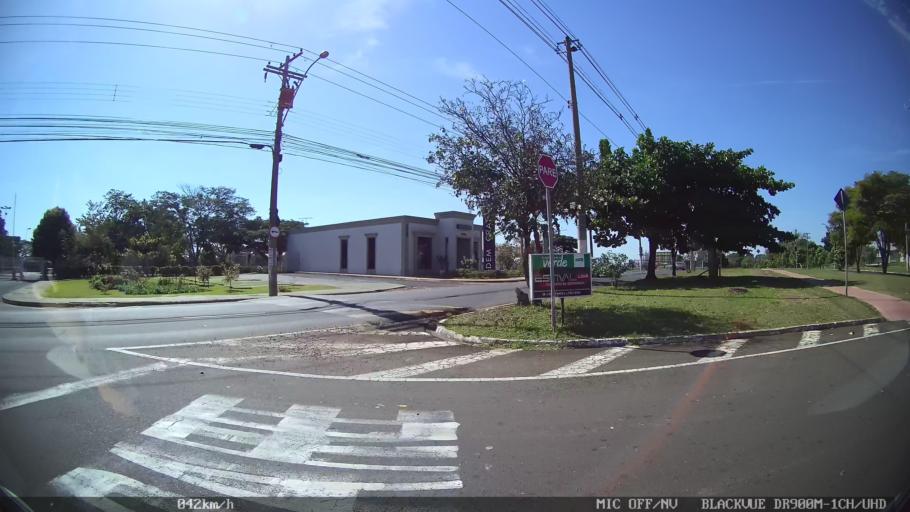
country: BR
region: Sao Paulo
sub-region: Franca
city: Franca
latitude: -20.5479
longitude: -47.4370
